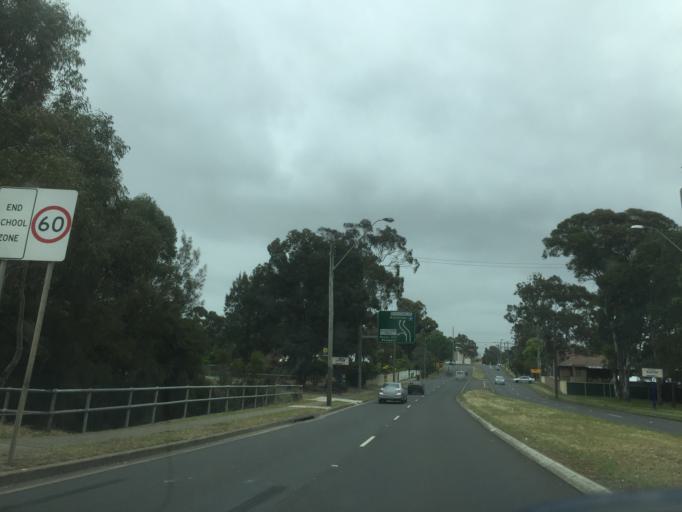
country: AU
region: New South Wales
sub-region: Blacktown
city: Blacktown
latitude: -33.7761
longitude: 150.9232
